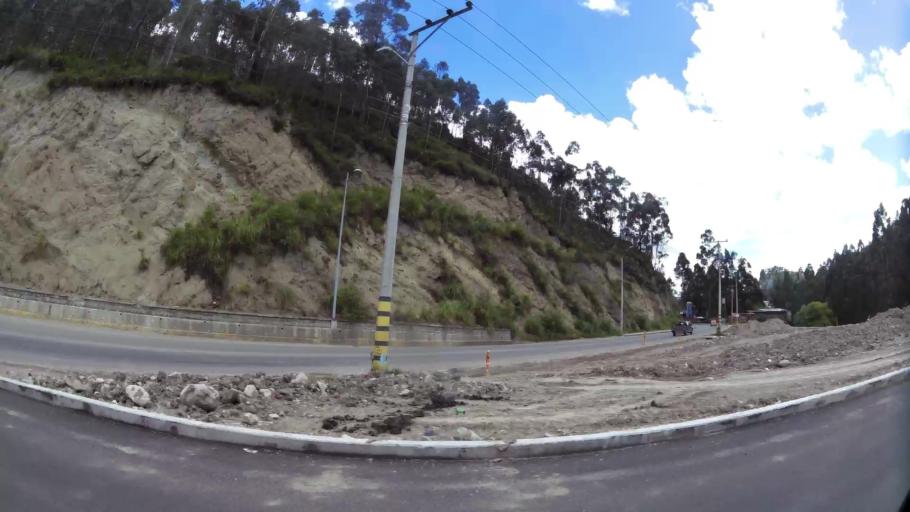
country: EC
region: Azuay
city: Cuenca
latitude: -2.9146
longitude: -78.9854
